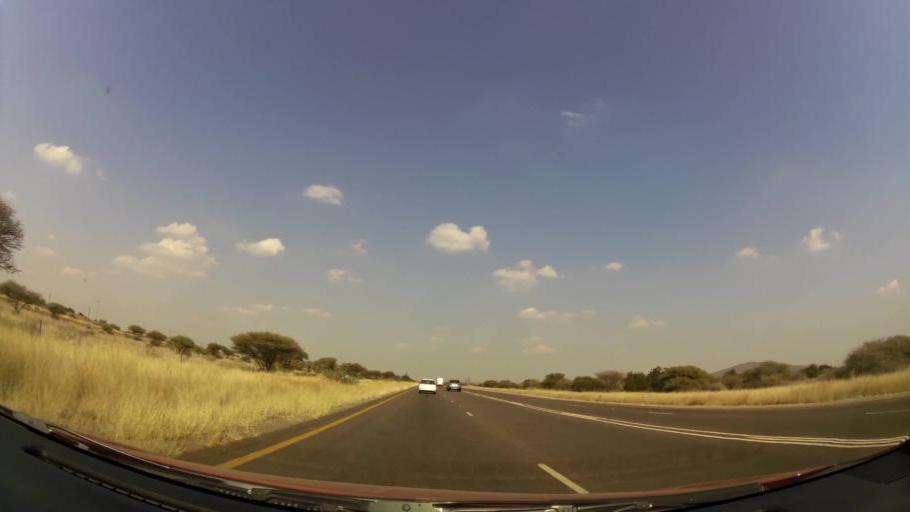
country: ZA
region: North-West
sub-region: Bojanala Platinum District Municipality
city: Mogwase
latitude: -25.4102
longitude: 27.0761
